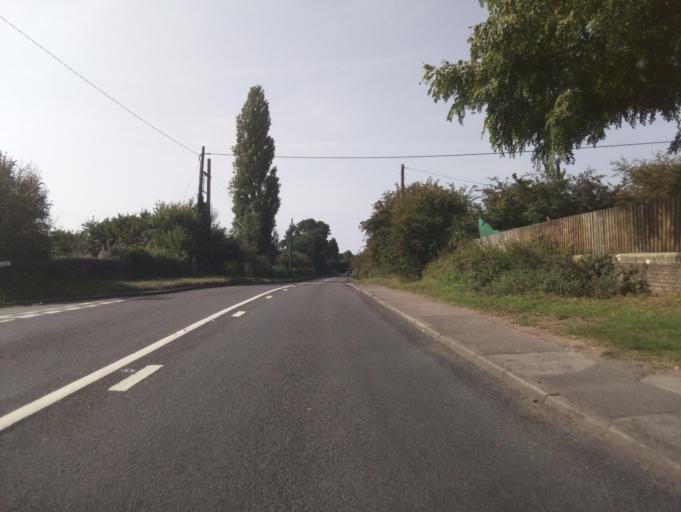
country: GB
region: England
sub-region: Staffordshire
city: Chasetown
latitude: 52.6606
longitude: -1.8761
